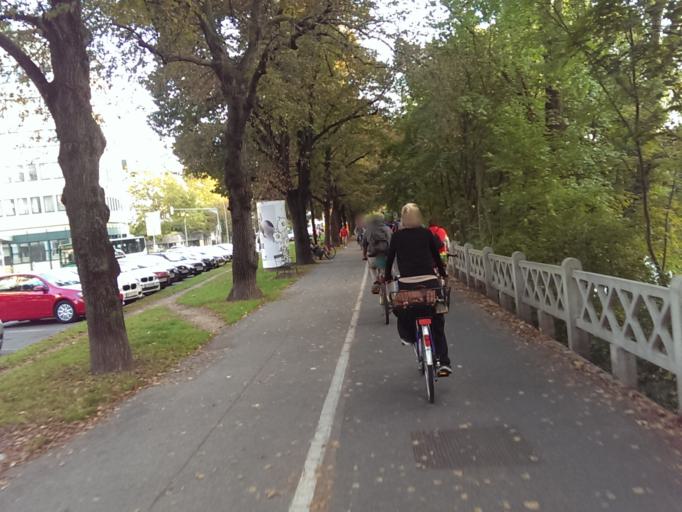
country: AT
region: Styria
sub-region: Graz Stadt
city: Graz
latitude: 47.0661
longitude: 15.4354
